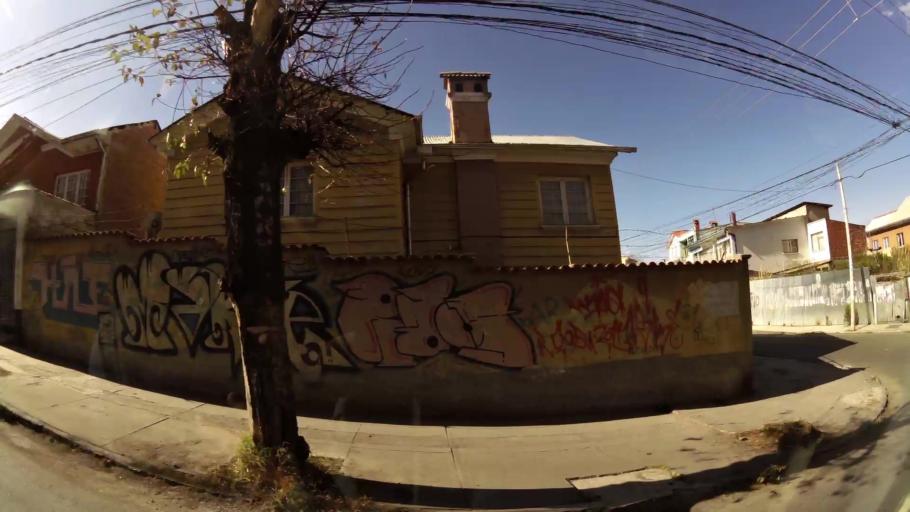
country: BO
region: La Paz
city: La Paz
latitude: -16.5169
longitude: -68.1311
